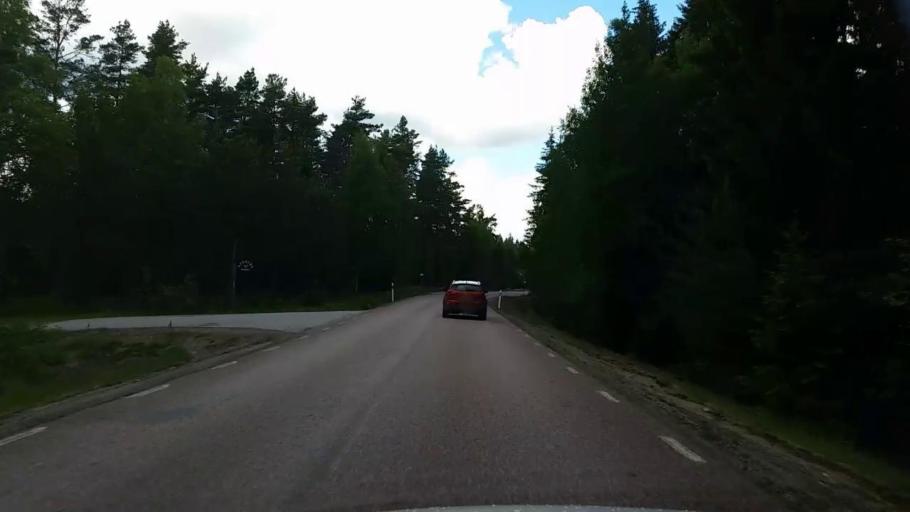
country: SE
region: Vaestmanland
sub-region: Fagersta Kommun
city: Fagersta
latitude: 59.8778
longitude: 15.8374
